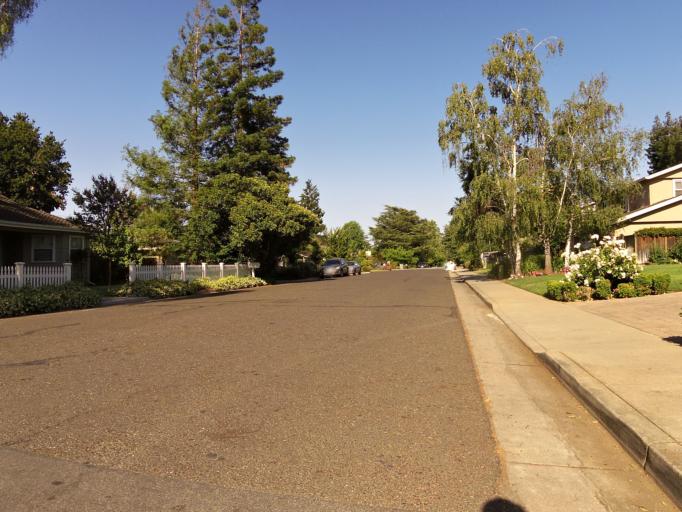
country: US
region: California
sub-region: Santa Clara County
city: Los Altos
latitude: 37.3813
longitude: -122.1108
